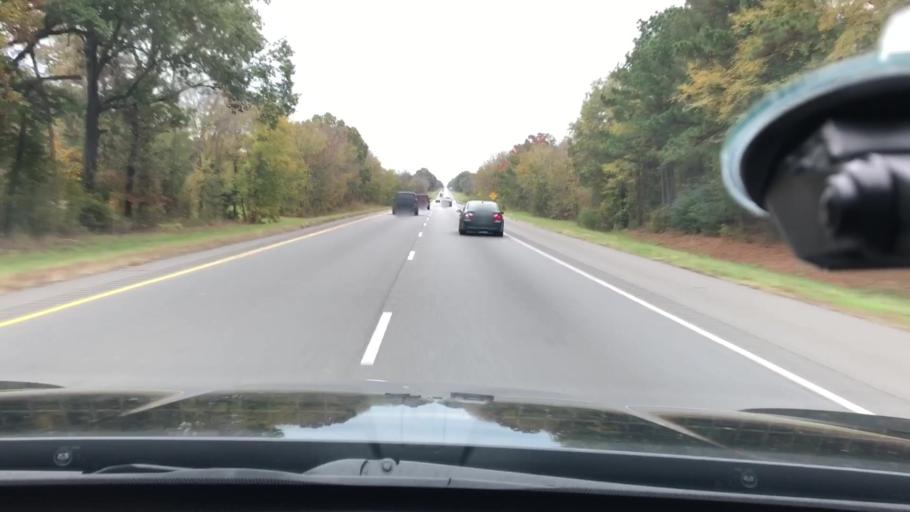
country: US
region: Arkansas
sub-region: Hempstead County
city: Hope
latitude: 33.6383
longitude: -93.7028
